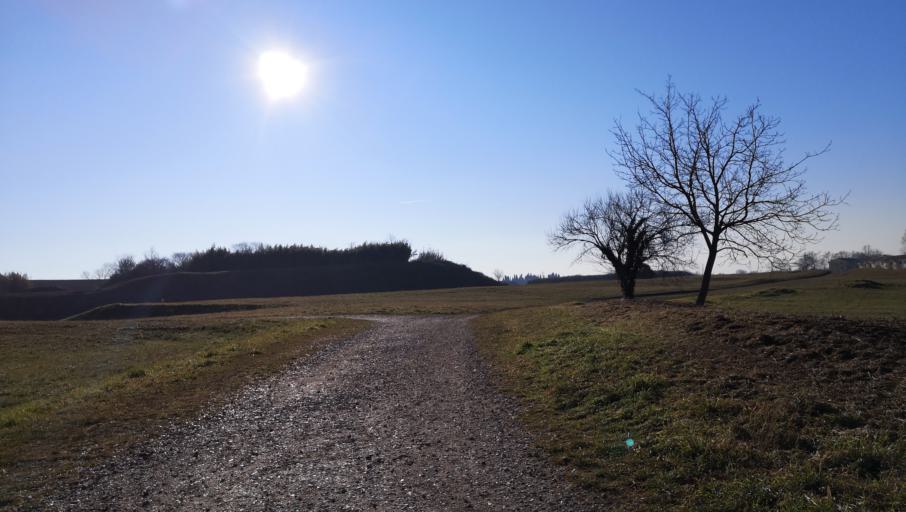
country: IT
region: Friuli Venezia Giulia
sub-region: Provincia di Udine
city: Palmanova
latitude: 45.9081
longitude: 13.3020
